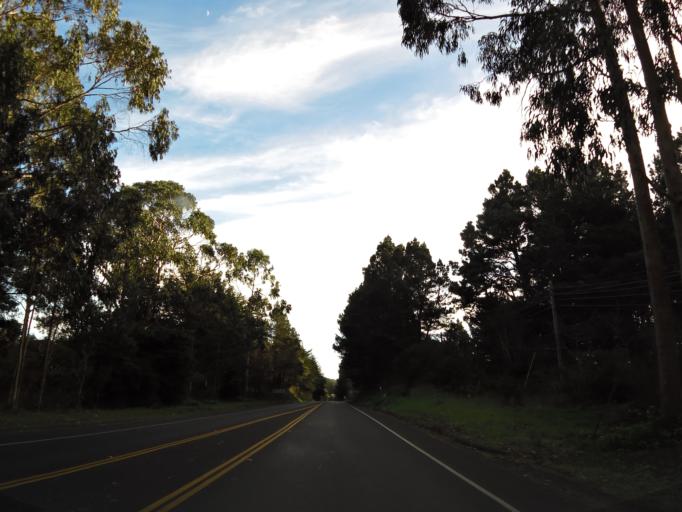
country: US
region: California
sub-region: Mendocino County
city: Fort Bragg
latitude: 39.3245
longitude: -123.8027
